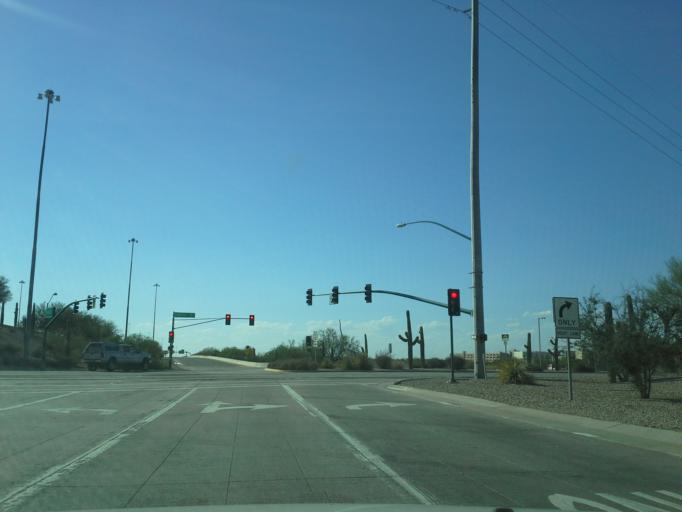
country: US
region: Arizona
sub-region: Maricopa County
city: Paradise Valley
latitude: 33.6683
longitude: -111.9595
